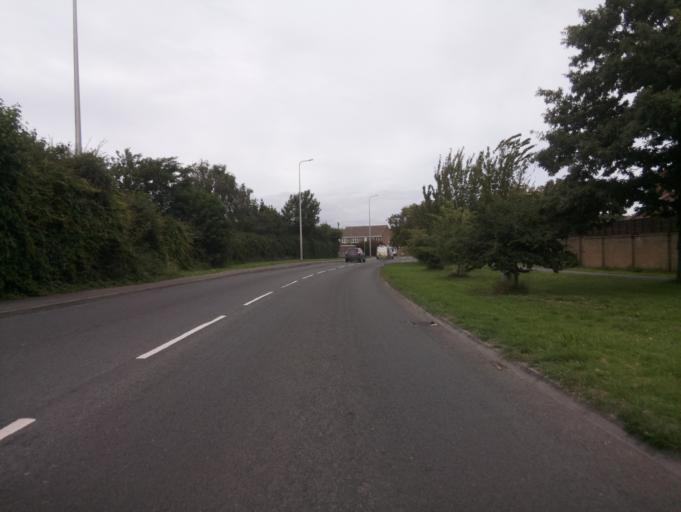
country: GB
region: England
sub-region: North Somerset
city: Kenn
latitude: 51.4254
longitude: -2.8547
